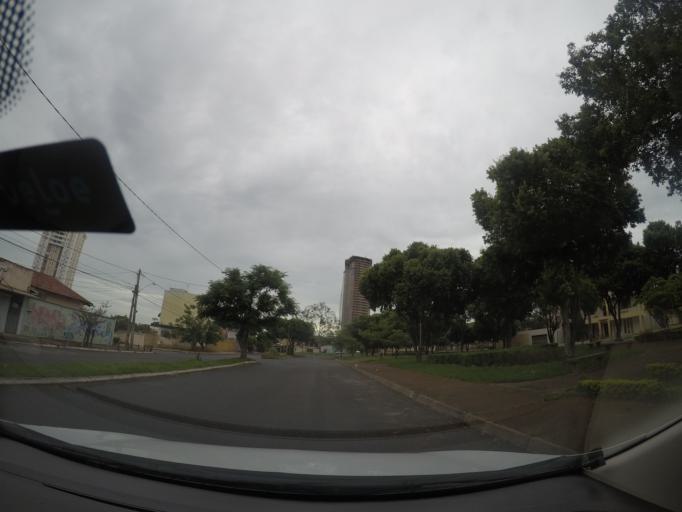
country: BR
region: Goias
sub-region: Goiania
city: Goiania
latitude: -16.6837
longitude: -49.2425
